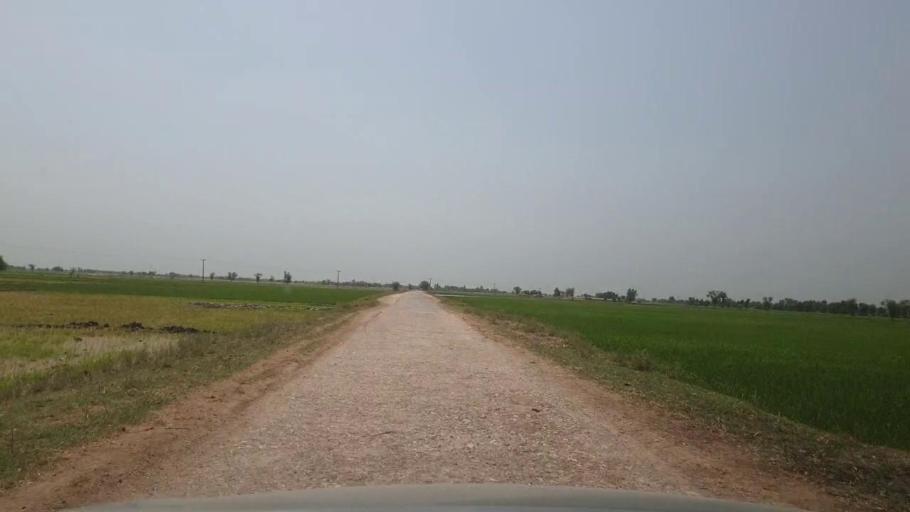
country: PK
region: Sindh
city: Garhi Yasin
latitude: 27.9198
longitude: 68.4040
